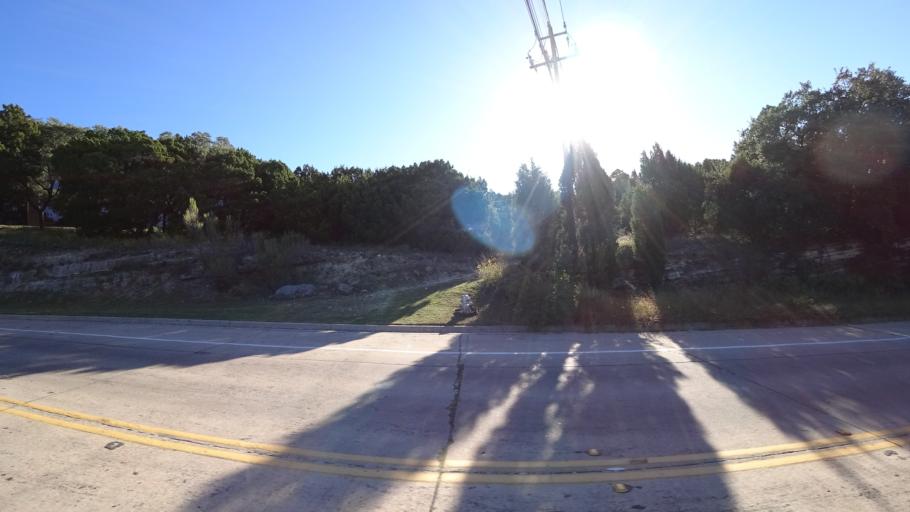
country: US
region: Texas
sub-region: Travis County
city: West Lake Hills
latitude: 30.3550
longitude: -97.7971
